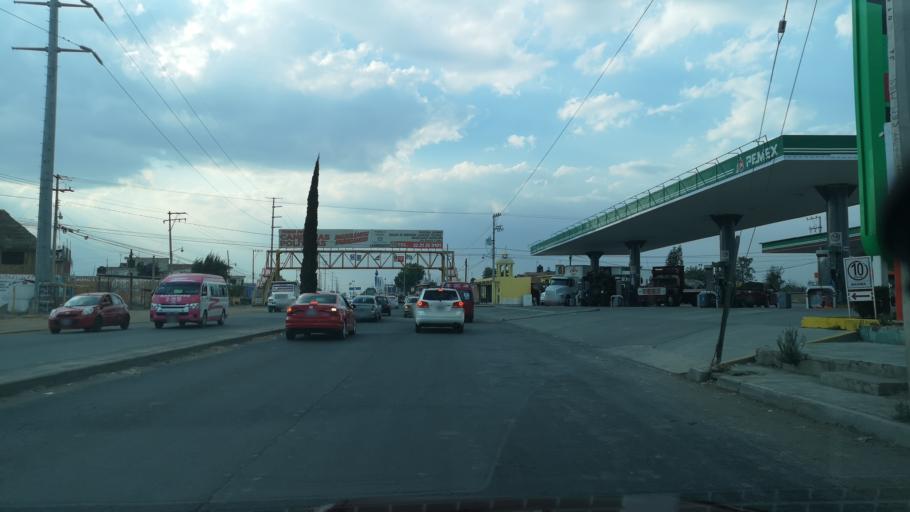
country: MX
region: Puebla
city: Cuanala
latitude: 19.0812
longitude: -98.3279
